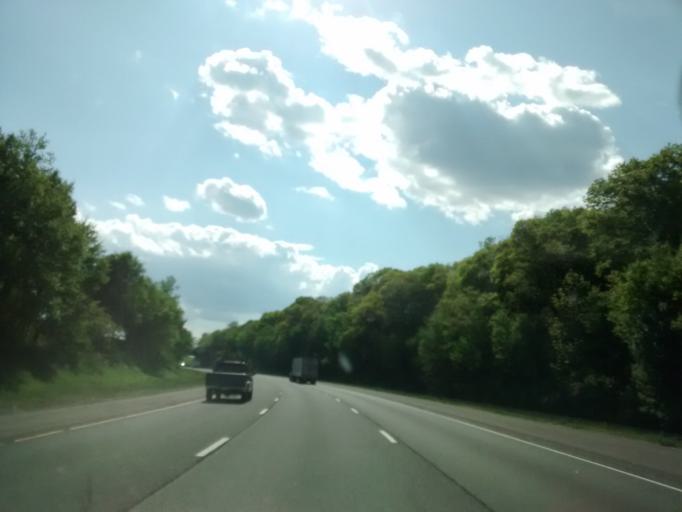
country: US
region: Connecticut
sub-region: Tolland County
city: Tolland
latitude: 41.8561
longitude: -72.4006
